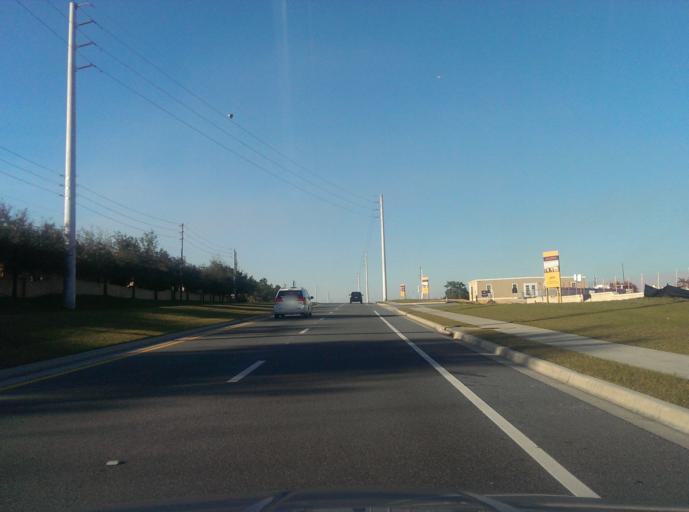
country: US
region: Florida
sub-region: Polk County
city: Citrus Ridge
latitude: 28.3235
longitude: -81.5907
